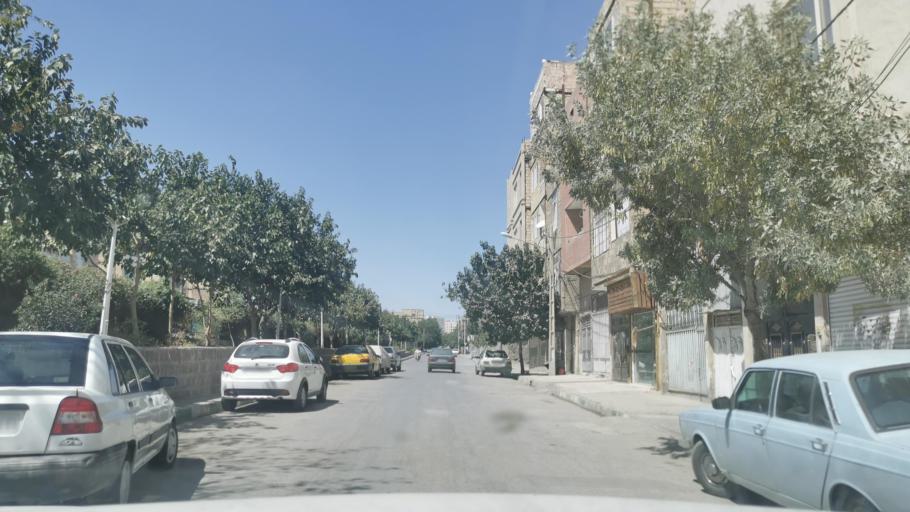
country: IR
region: Razavi Khorasan
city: Mashhad
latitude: 36.3604
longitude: 59.5598
